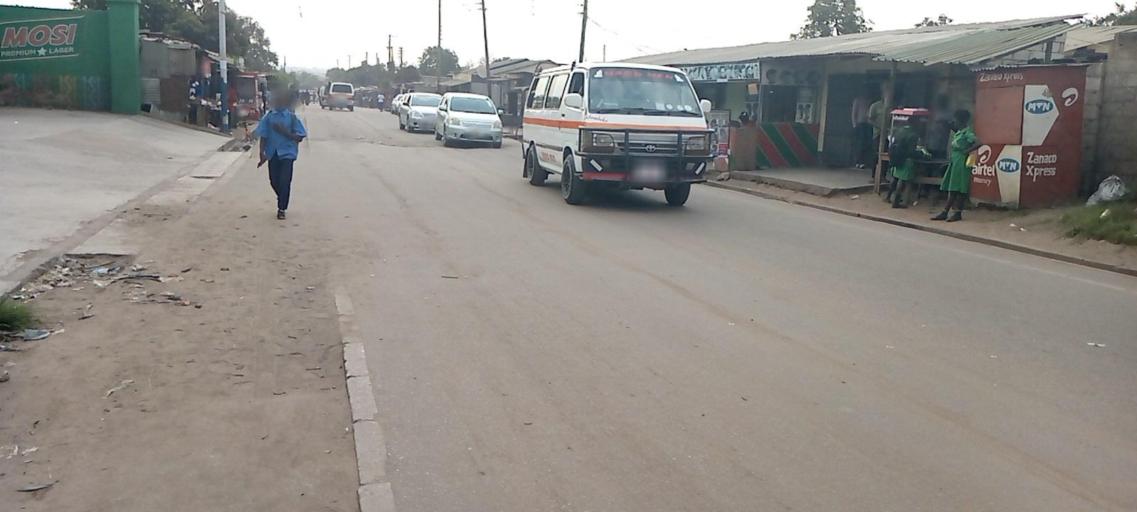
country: ZM
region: Lusaka
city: Lusaka
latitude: -15.4024
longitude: 28.3524
